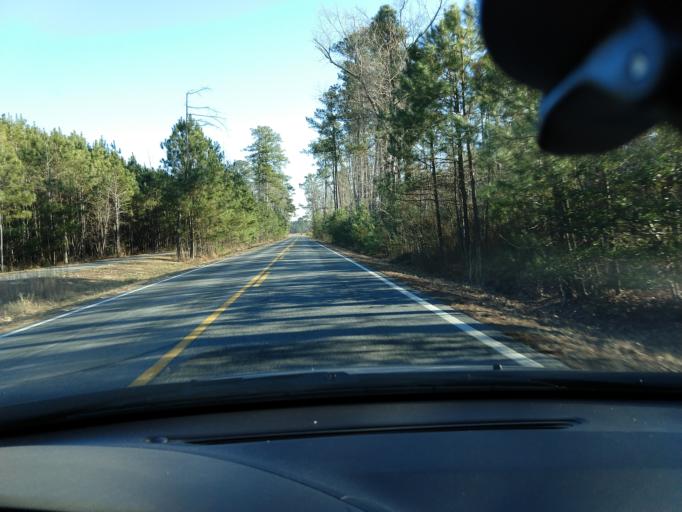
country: US
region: Virginia
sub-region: Charles City County
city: Charles City
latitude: 37.3064
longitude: -76.9596
